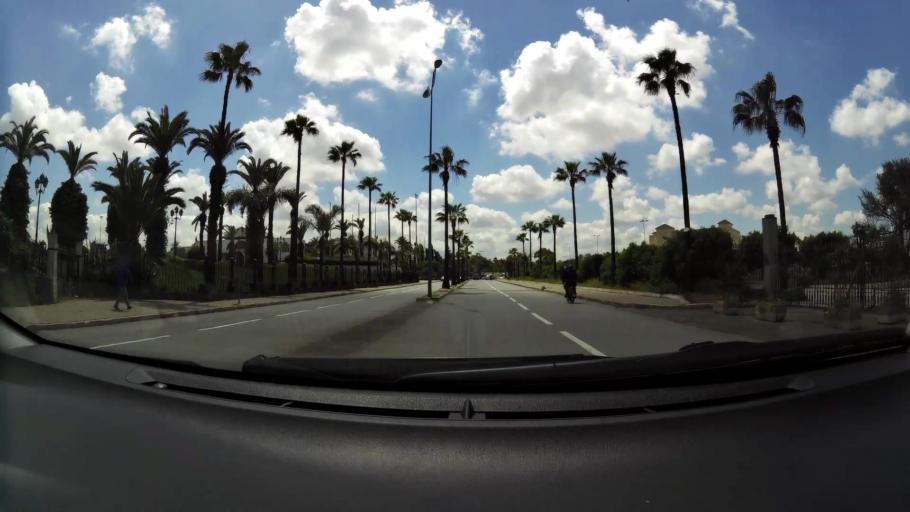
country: MA
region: Grand Casablanca
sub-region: Casablanca
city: Casablanca
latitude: 33.5590
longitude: -7.5637
